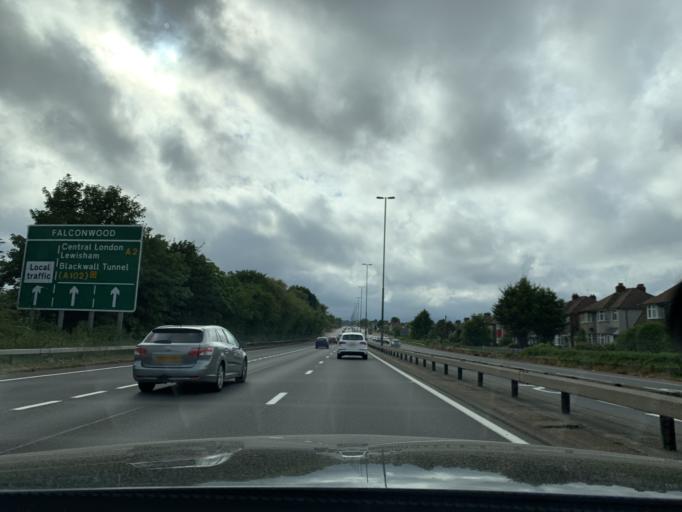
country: GB
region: England
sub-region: Greater London
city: Welling
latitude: 51.4530
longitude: 0.1000
